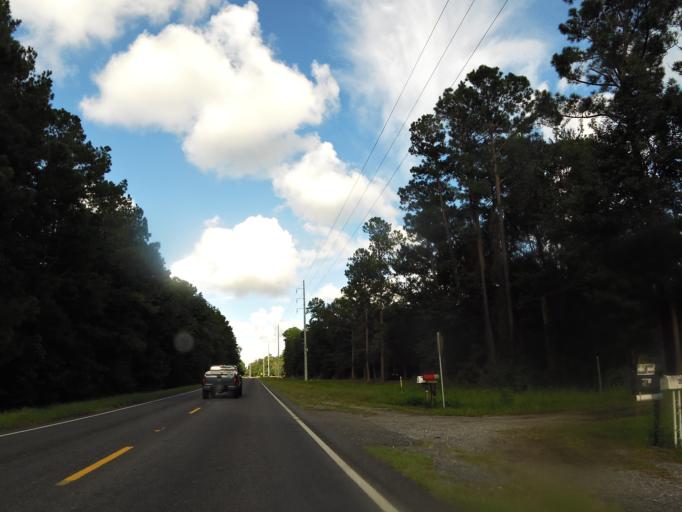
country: US
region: Georgia
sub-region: Glynn County
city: Brunswick
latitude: 31.1077
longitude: -81.6241
